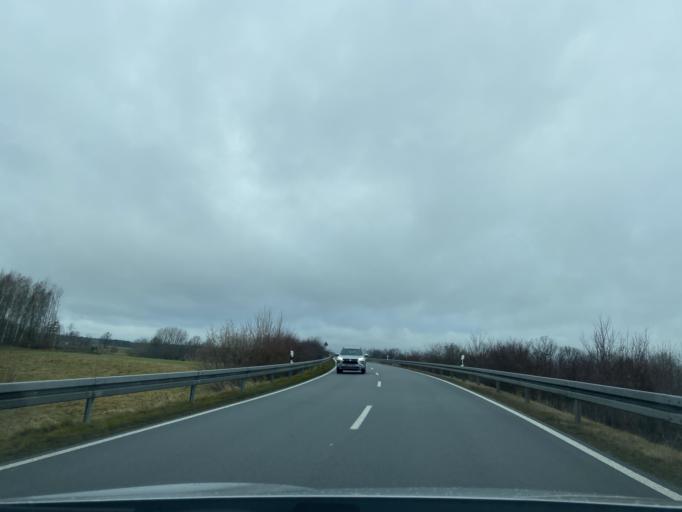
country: DE
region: Saxony
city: Kodersdorf
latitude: 51.2215
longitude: 14.9542
